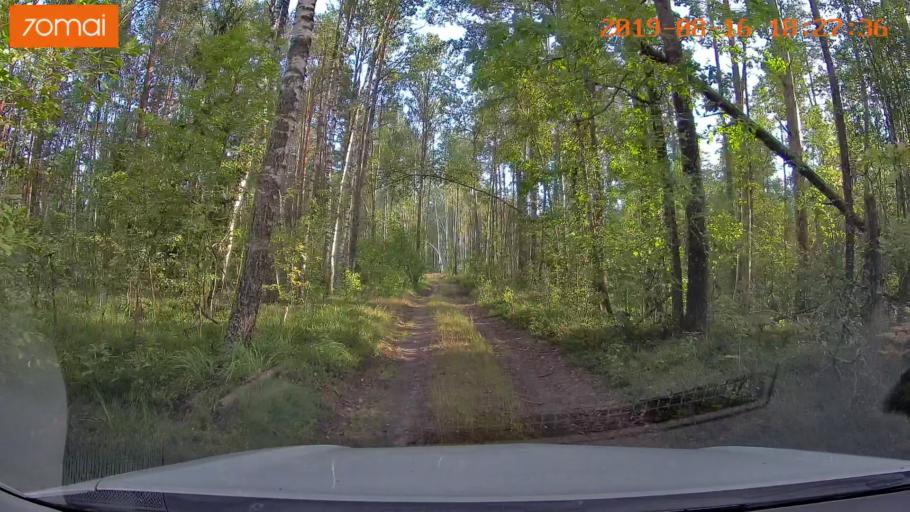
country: BY
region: Mogilev
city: Asipovichy
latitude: 53.2014
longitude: 28.6394
